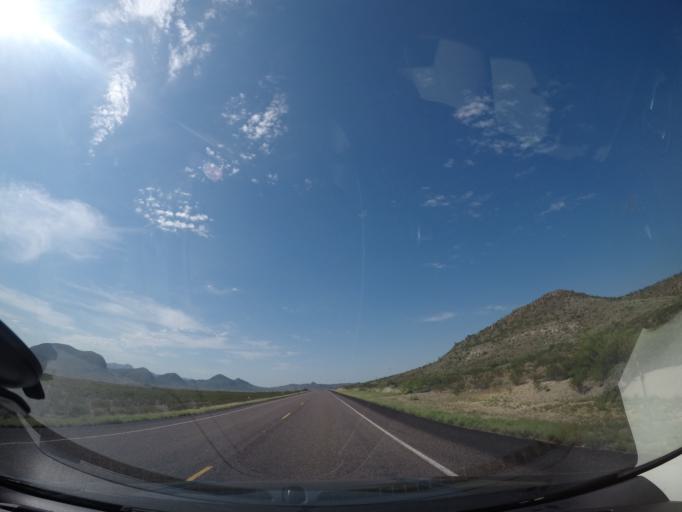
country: US
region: Texas
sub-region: Presidio County
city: Presidio
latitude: 29.5087
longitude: -103.5376
